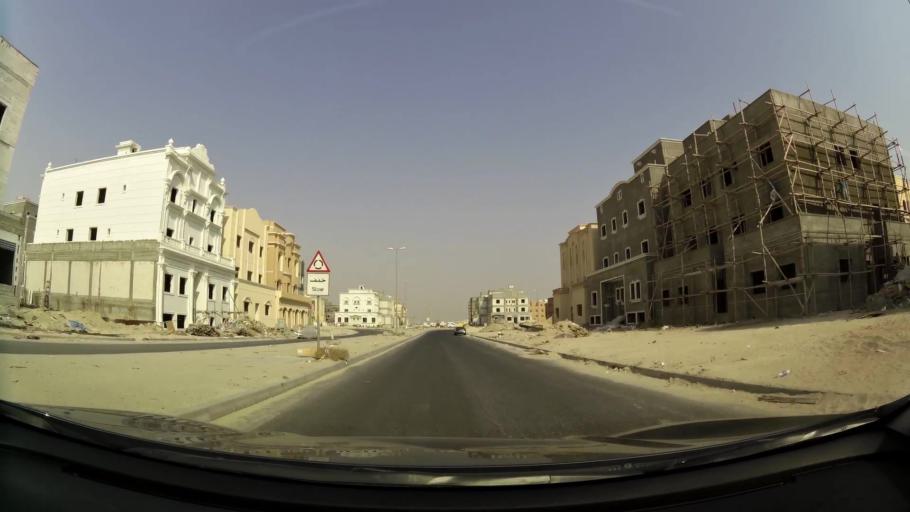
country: KW
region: Muhafazat al Jahra'
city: Al Jahra'
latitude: 29.3553
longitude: 47.7698
